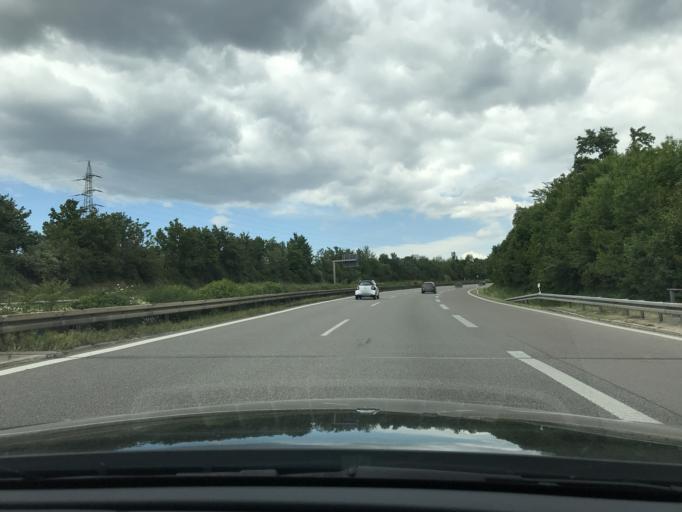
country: DE
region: Baden-Wuerttemberg
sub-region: Regierungsbezirk Stuttgart
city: Waiblingen
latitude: 48.8296
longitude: 9.3327
